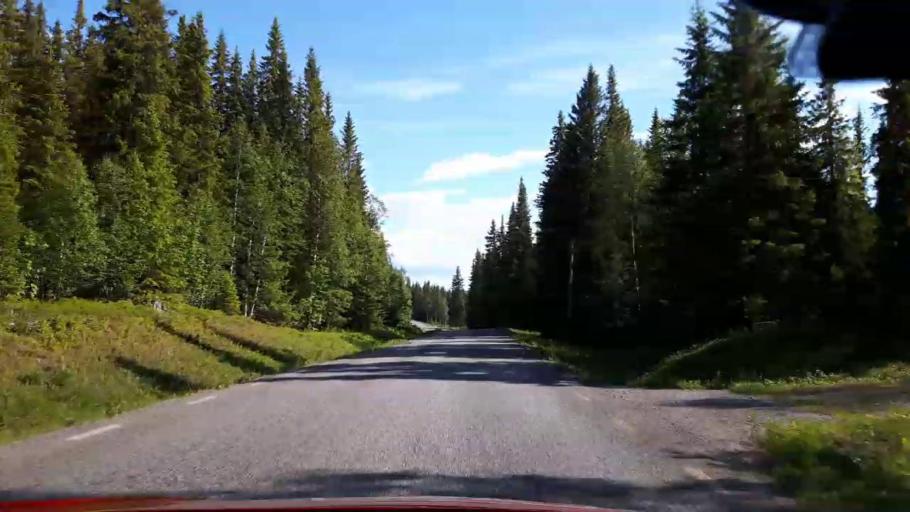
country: SE
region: Jaemtland
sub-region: Krokoms Kommun
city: Valla
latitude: 63.7263
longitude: 14.1220
